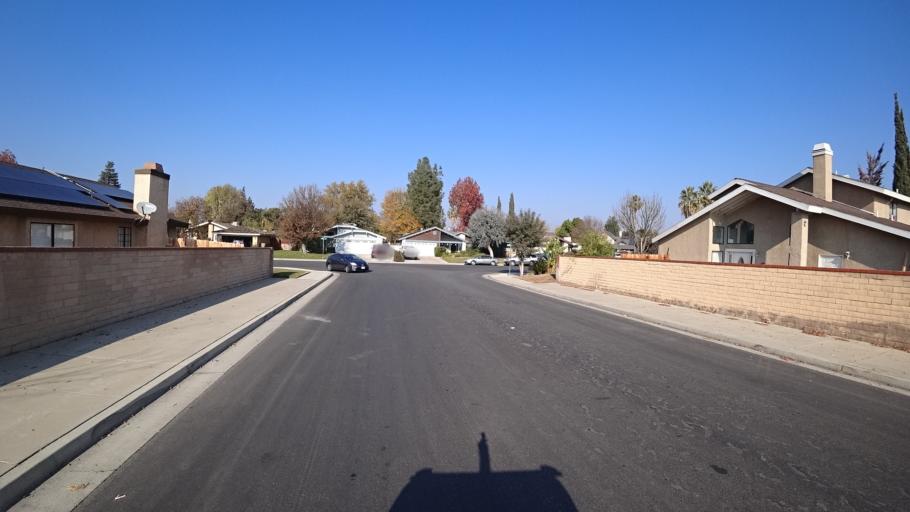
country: US
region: California
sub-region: Kern County
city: Greenacres
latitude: 35.3184
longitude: -119.0865
